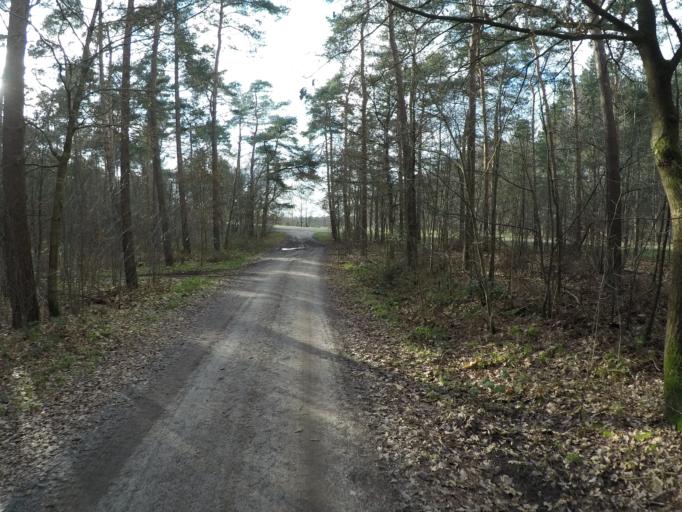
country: BE
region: Flanders
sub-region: Provincie Antwerpen
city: Vorselaar
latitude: 51.2488
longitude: 4.7760
